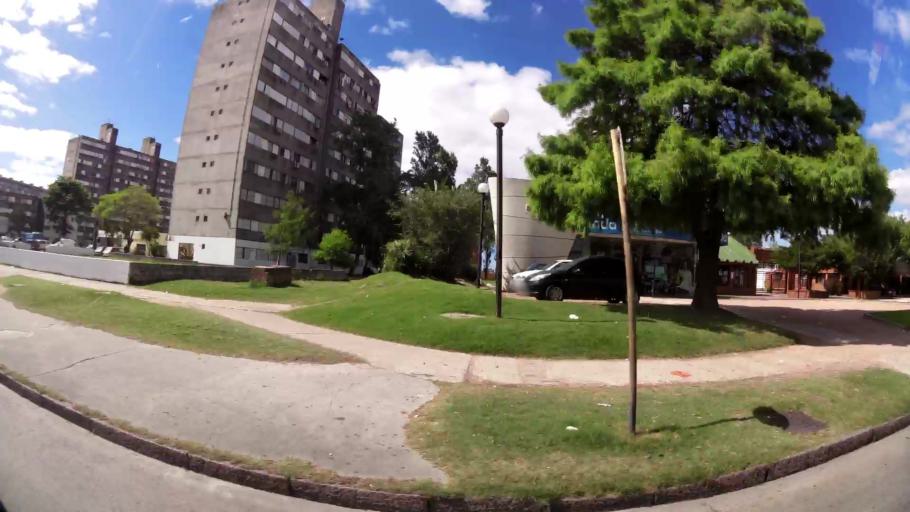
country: UY
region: Canelones
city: Paso de Carrasco
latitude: -34.8720
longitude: -56.1195
